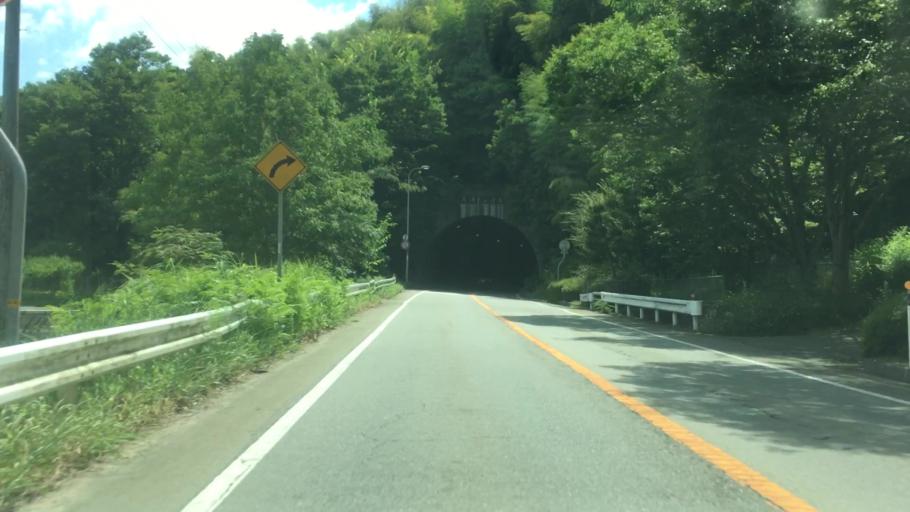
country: JP
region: Hyogo
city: Toyooka
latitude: 35.4664
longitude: 134.7563
